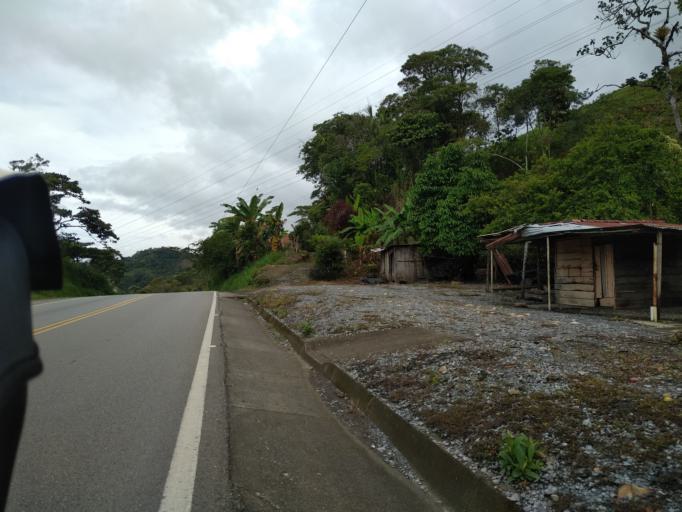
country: CO
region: Santander
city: Suaita
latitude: 6.1249
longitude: -73.3638
